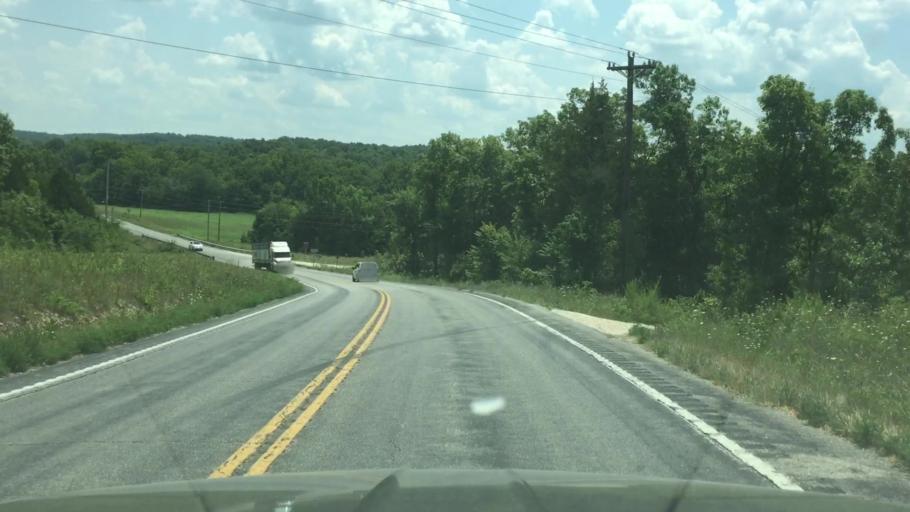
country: US
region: Missouri
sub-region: Miller County
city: Tuscumbia
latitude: 38.0871
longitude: -92.4967
